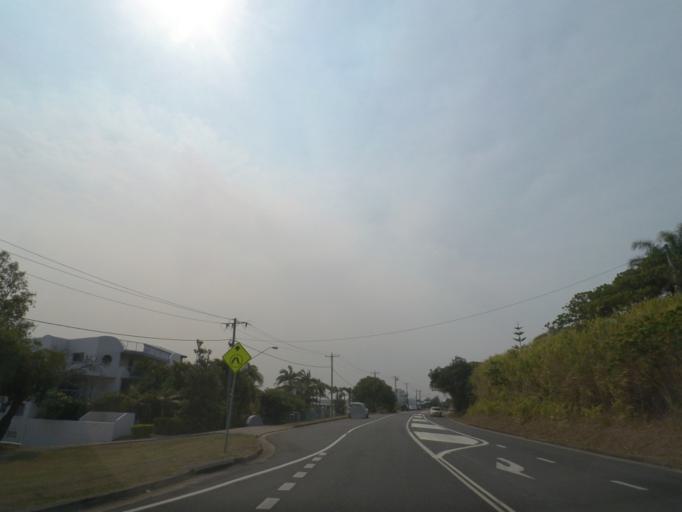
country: AU
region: New South Wales
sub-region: Tweed
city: Casuarina
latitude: -28.3337
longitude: 153.5709
